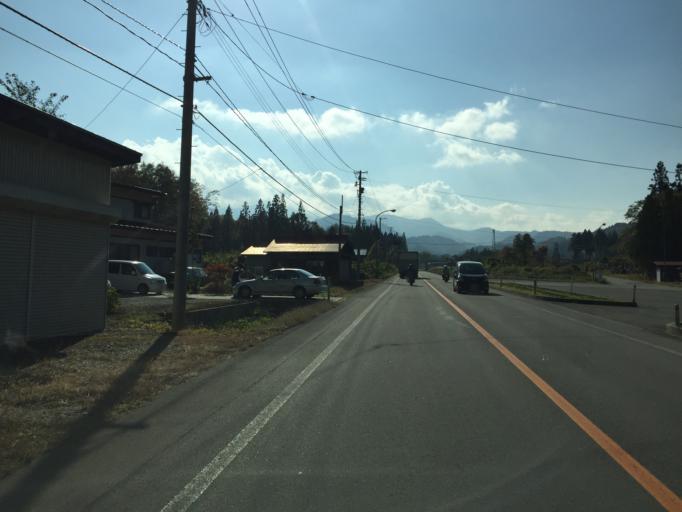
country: JP
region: Yamagata
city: Yonezawa
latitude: 37.8929
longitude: 140.0104
